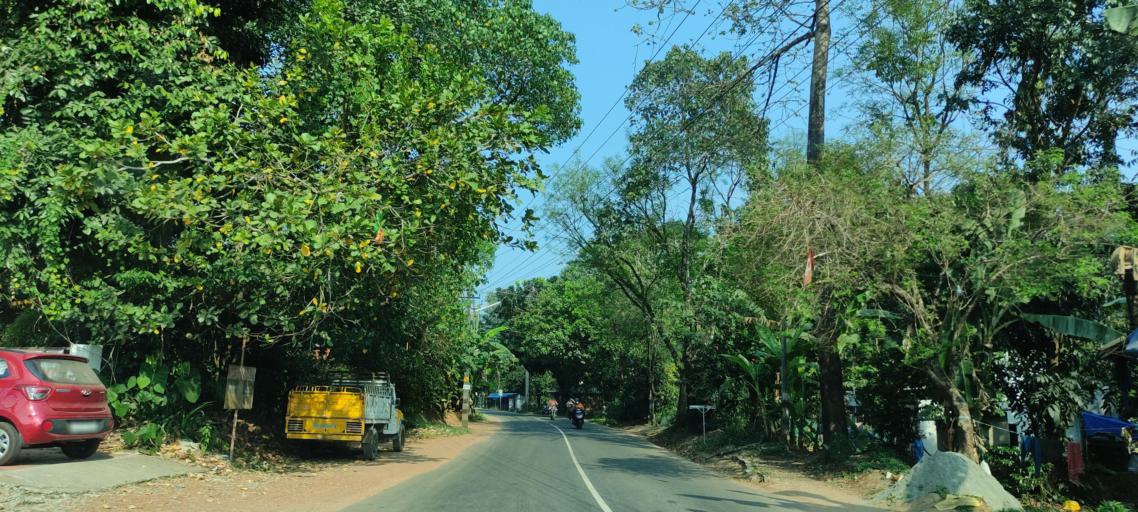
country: IN
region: Kerala
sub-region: Pattanamtitta
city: Adur
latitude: 9.0688
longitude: 76.6514
